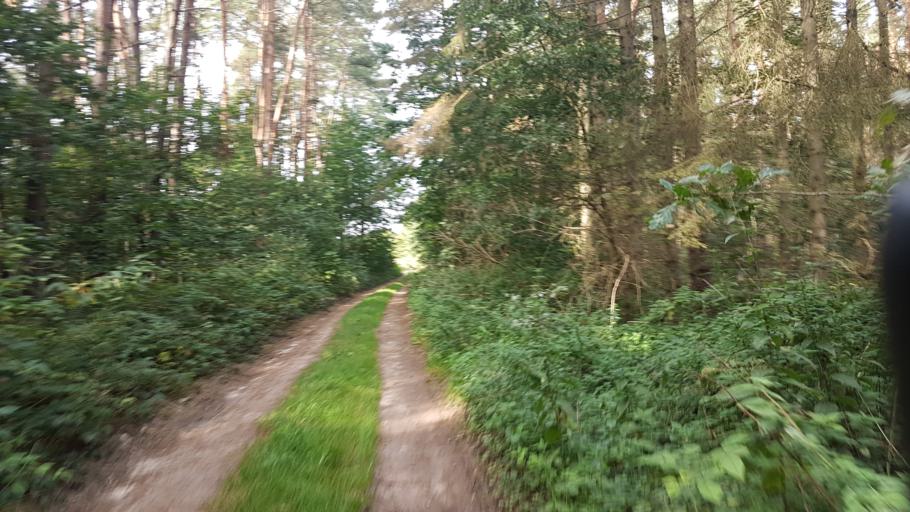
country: DE
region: Mecklenburg-Vorpommern
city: Samtens
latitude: 54.3725
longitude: 13.2831
